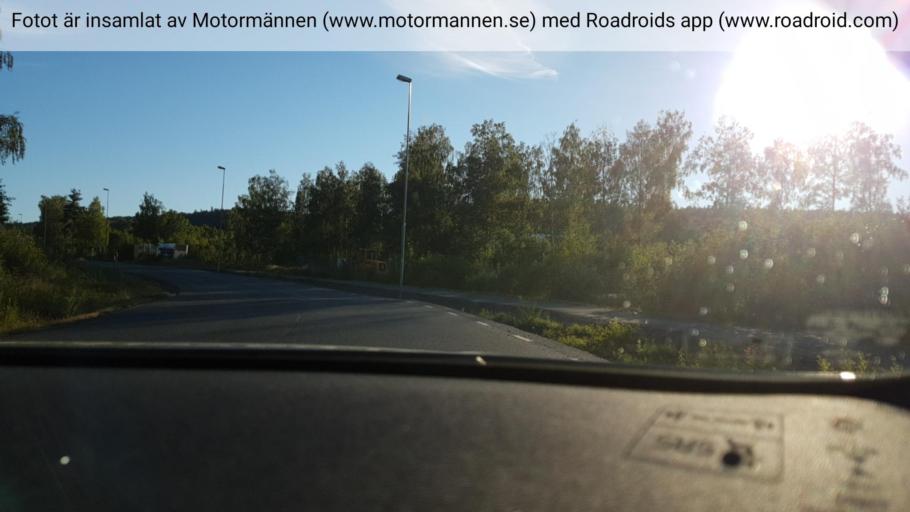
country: SE
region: Joenkoeping
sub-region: Jonkopings Kommun
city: Jonkoping
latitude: 57.7616
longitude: 14.1450
